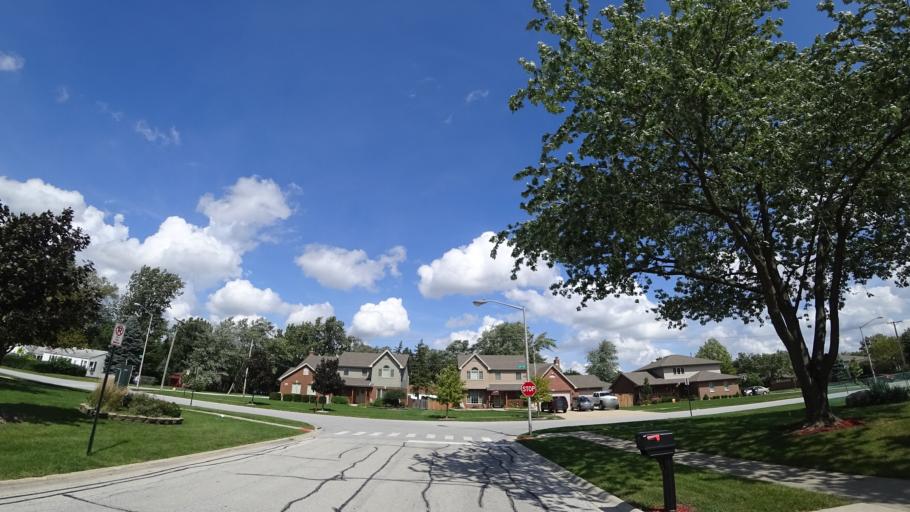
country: US
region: Illinois
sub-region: Cook County
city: Tinley Park
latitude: 41.5657
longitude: -87.7799
